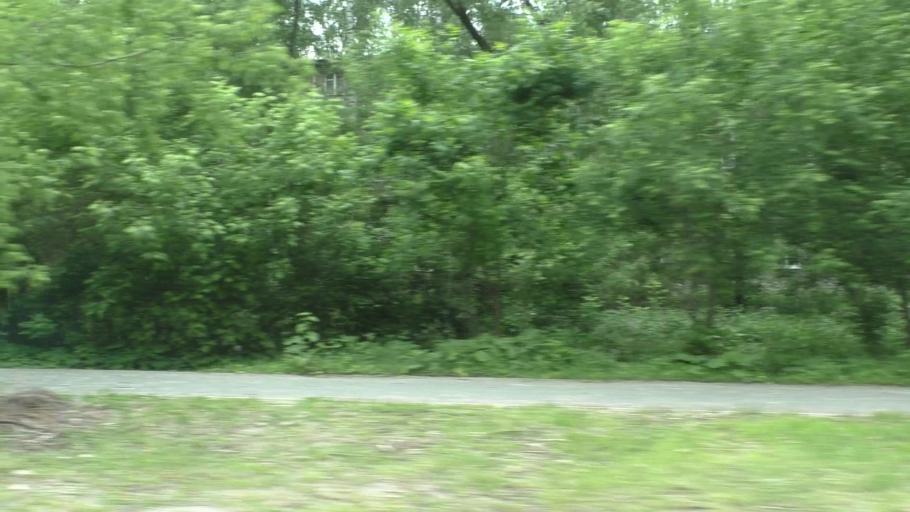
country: RU
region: Moskovskaya
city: Yegor'yevsk
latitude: 55.3689
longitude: 39.0537
